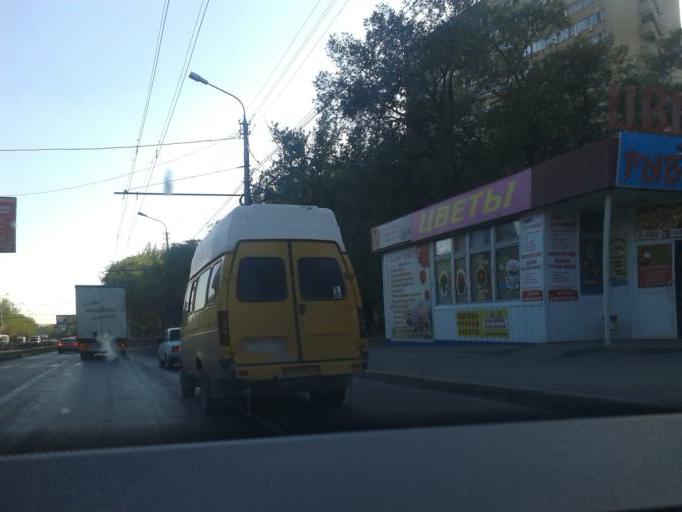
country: RU
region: Volgograd
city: Volgograd
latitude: 48.6189
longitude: 44.4239
